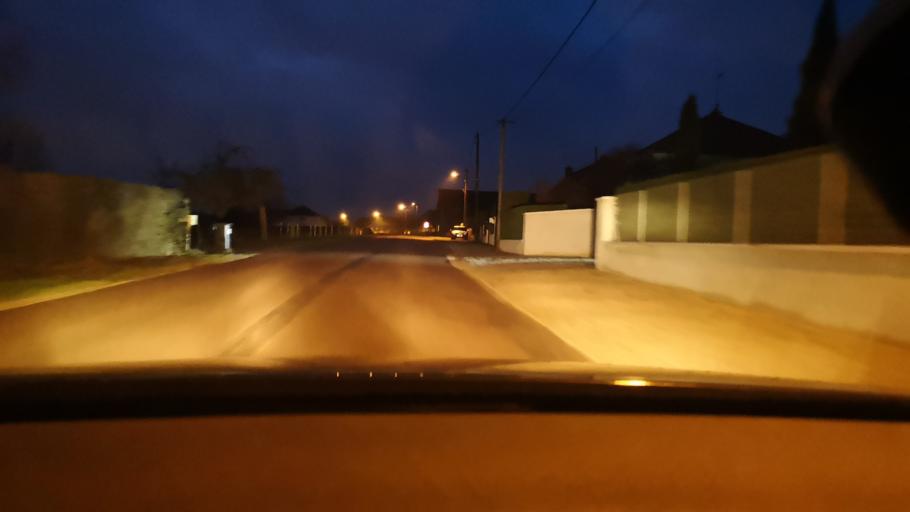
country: FR
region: Bourgogne
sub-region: Departement de Saone-et-Loire
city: Champforgeuil
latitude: 46.8399
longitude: 4.8112
